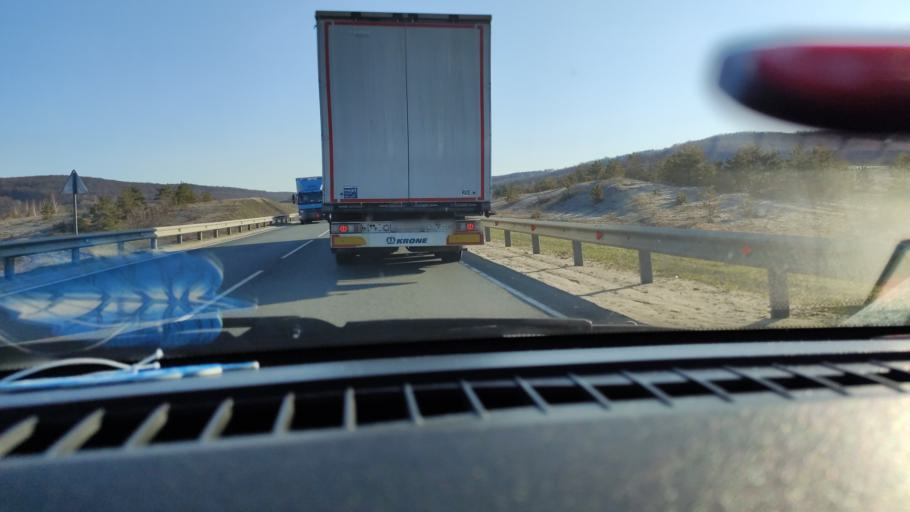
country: RU
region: Saratov
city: Alekseyevka
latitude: 52.3958
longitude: 47.9840
